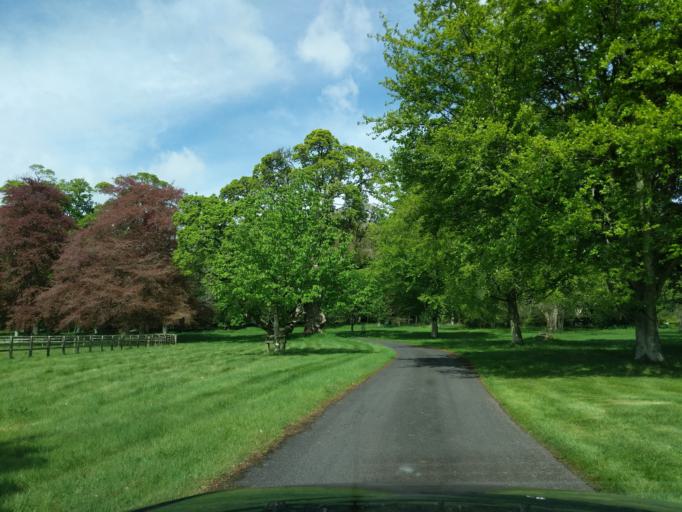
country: GB
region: Scotland
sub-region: The Scottish Borders
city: Saint Boswells
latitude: 55.6446
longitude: -2.5637
